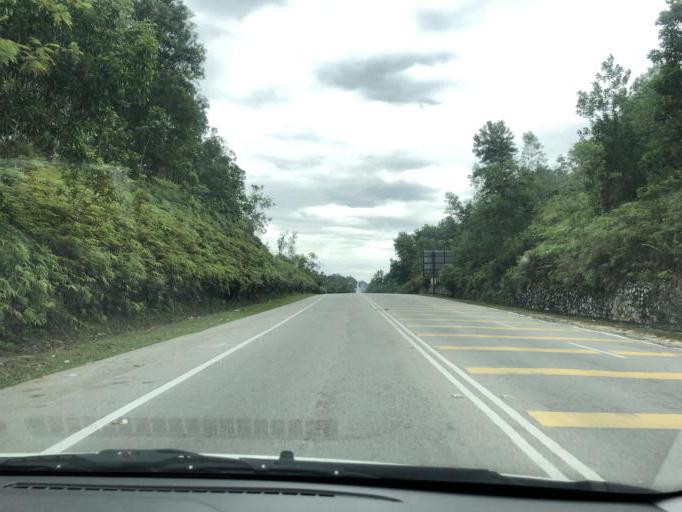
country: MY
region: Putrajaya
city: Putrajaya
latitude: 2.9231
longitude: 101.7472
